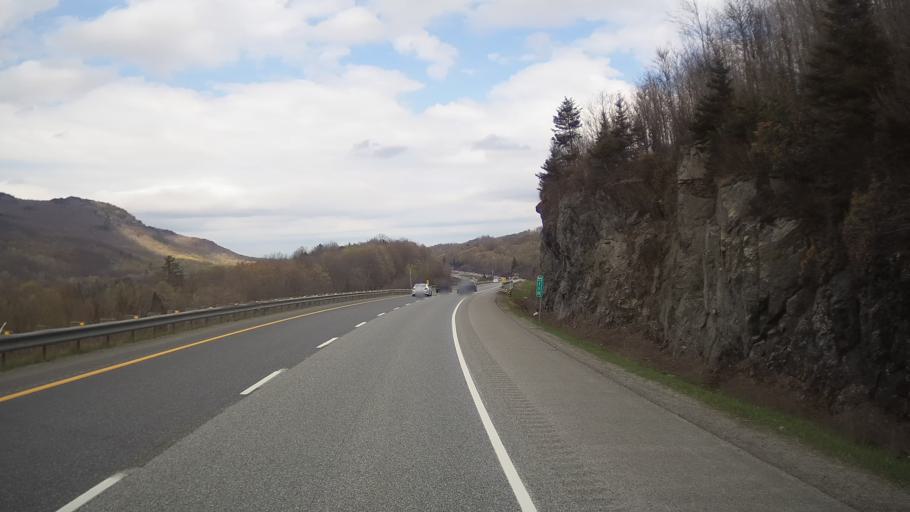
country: CA
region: Quebec
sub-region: Estrie
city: Magog
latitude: 45.2896
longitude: -72.2645
